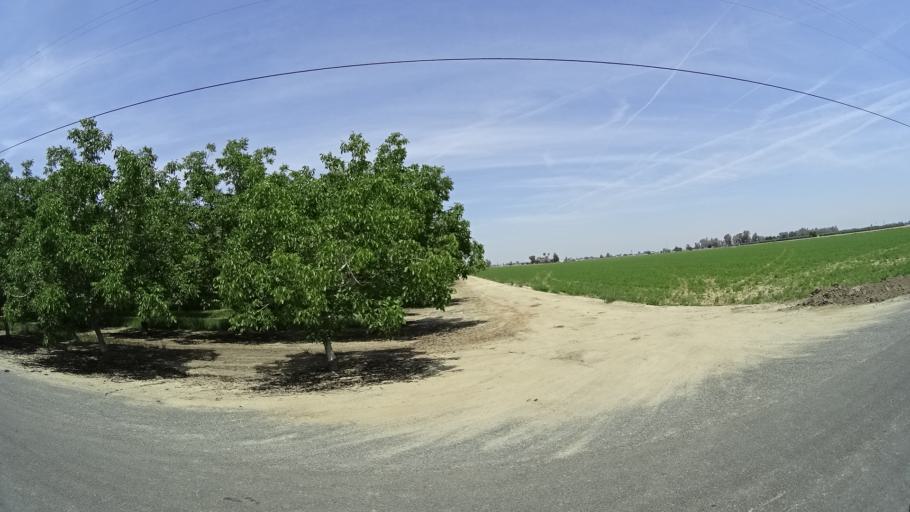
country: US
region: California
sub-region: Fresno County
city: Riverdale
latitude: 36.3947
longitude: -119.8571
